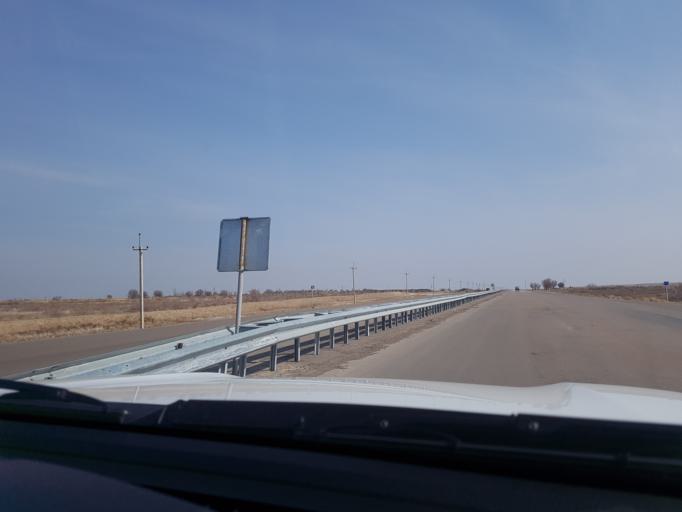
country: TM
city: Akdepe
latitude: 41.7375
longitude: 59.1555
